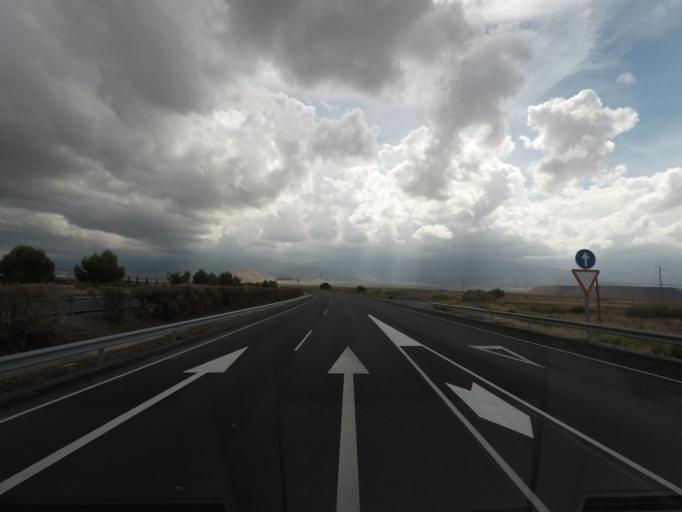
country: ES
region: Andalusia
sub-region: Provincia de Granada
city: Albunan
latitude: 37.2286
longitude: -3.0821
